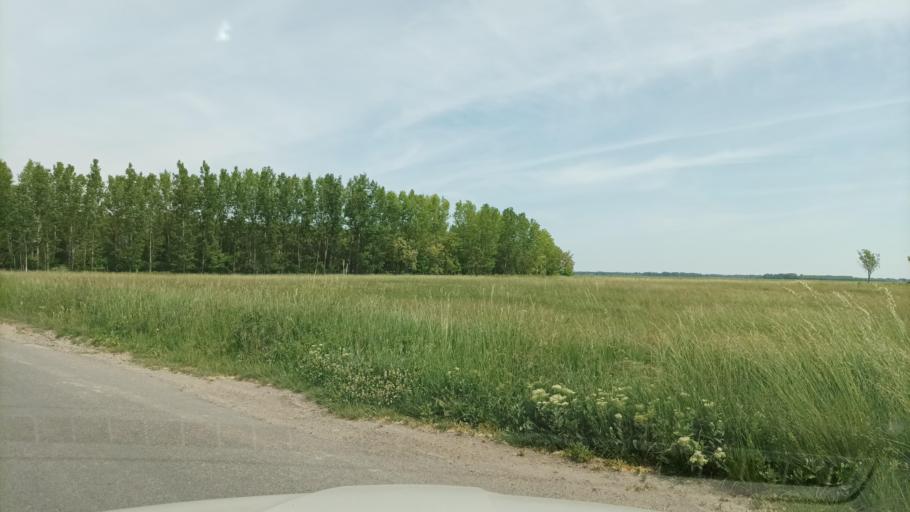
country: HU
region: Fejer
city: Racalmas
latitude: 47.0773
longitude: 18.9420
